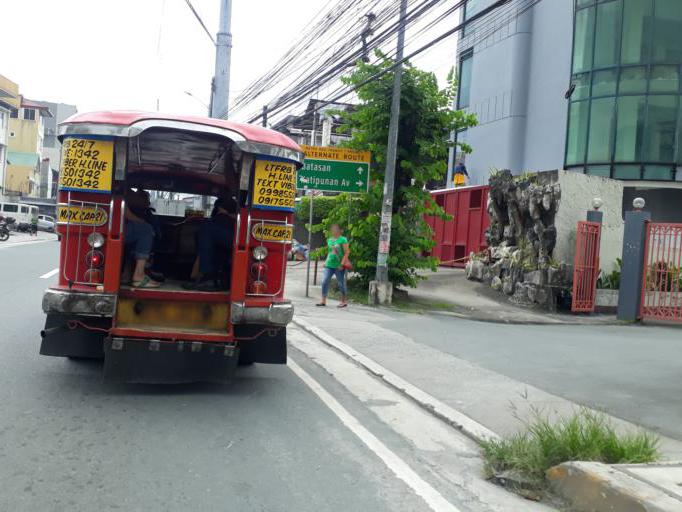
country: PH
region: Calabarzon
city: Bagong Pagasa
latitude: 14.6782
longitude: 121.0295
